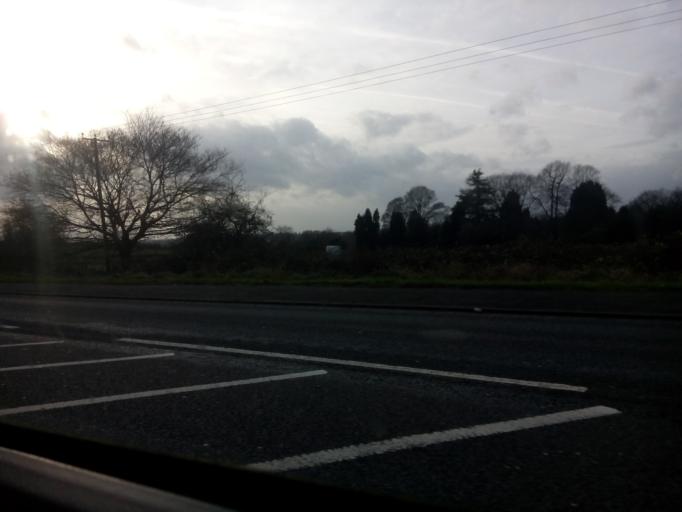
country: GB
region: England
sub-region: Worcestershire
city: Bromsgrove
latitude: 52.3738
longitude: -2.0457
